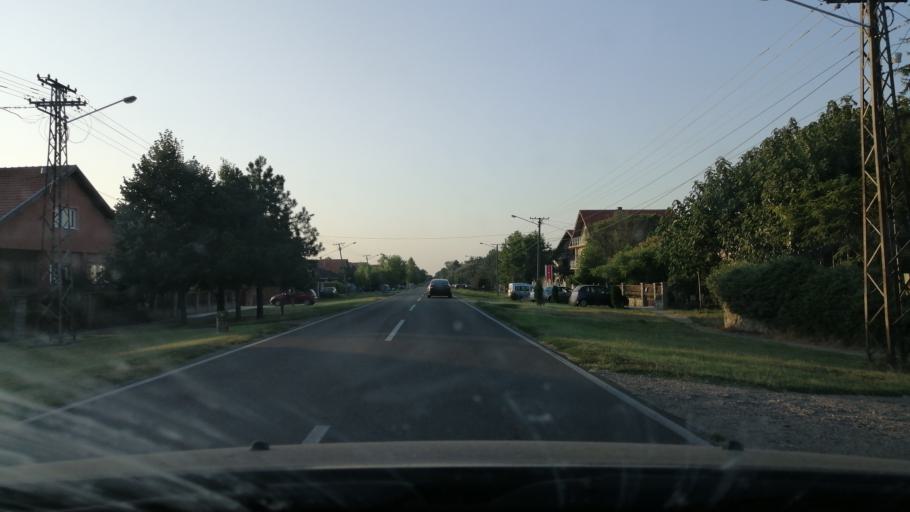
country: RS
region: Central Serbia
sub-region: Belgrade
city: Grocka
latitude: 44.7676
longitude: 20.7304
